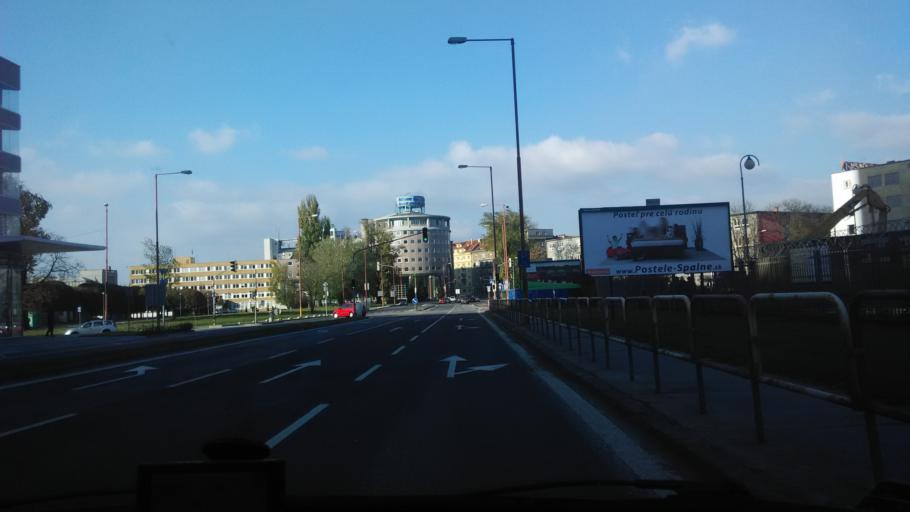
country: SK
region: Bratislavsky
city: Bratislava
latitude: 48.1426
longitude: 17.1256
